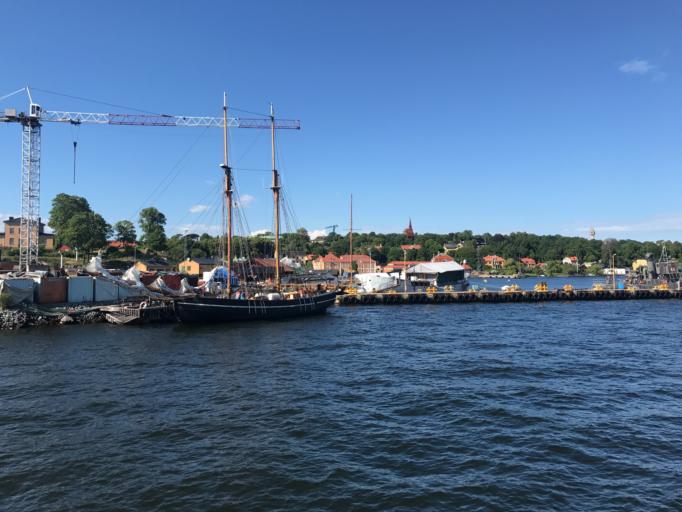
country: SE
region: Stockholm
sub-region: Stockholms Kommun
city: OEstermalm
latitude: 59.3191
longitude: 18.1018
